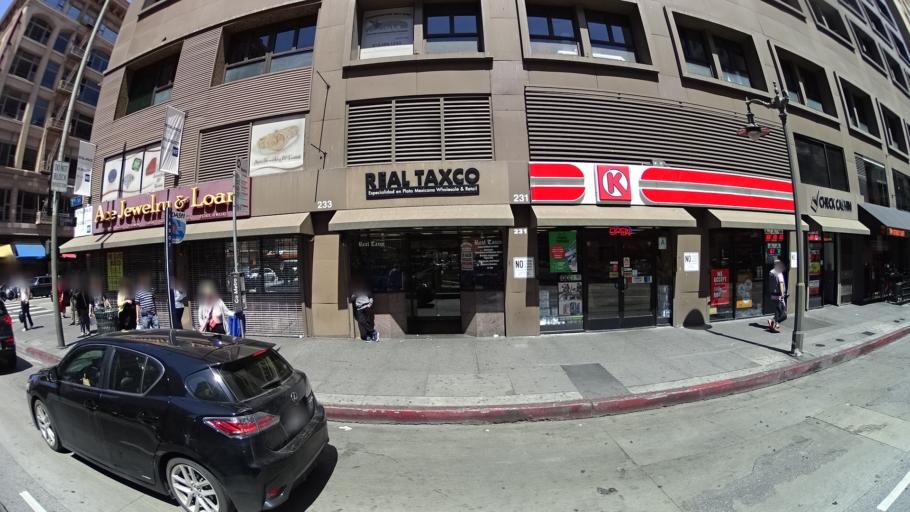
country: US
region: California
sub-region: Los Angeles County
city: Los Angeles
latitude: 34.0451
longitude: -118.2532
